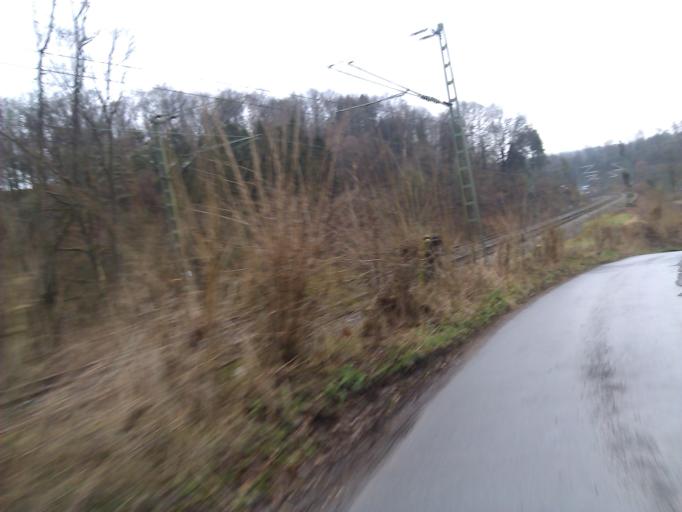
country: DE
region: North Rhine-Westphalia
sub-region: Regierungsbezirk Dusseldorf
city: Heiligenhaus
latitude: 51.3462
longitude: 6.9250
